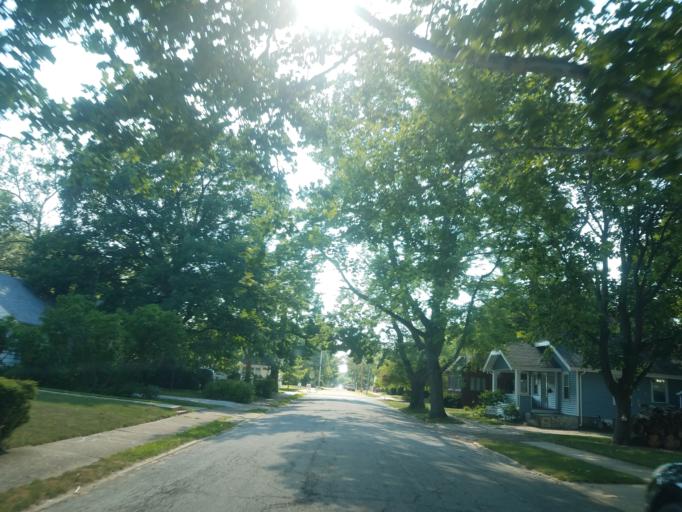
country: US
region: Illinois
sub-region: McLean County
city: Bloomington
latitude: 40.4762
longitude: -88.9711
